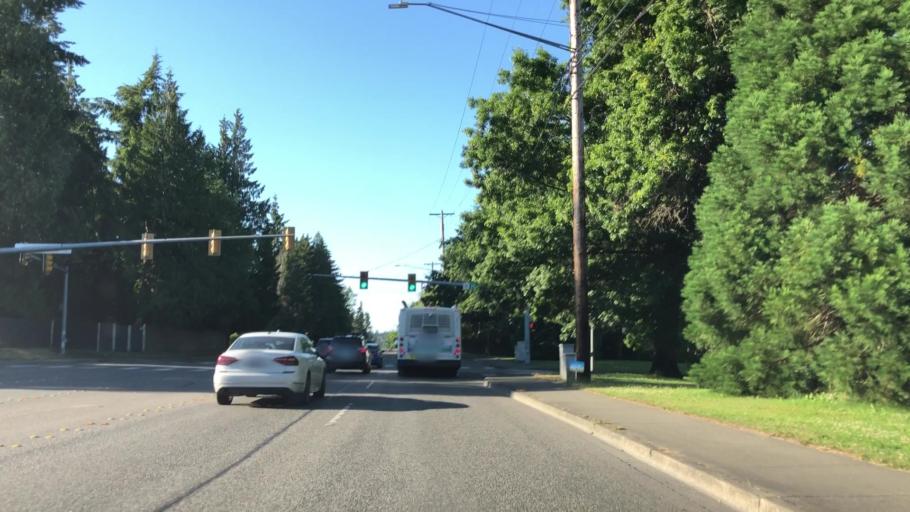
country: US
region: Washington
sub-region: Snohomish County
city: Mountlake Terrace
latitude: 47.8015
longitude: -122.2922
